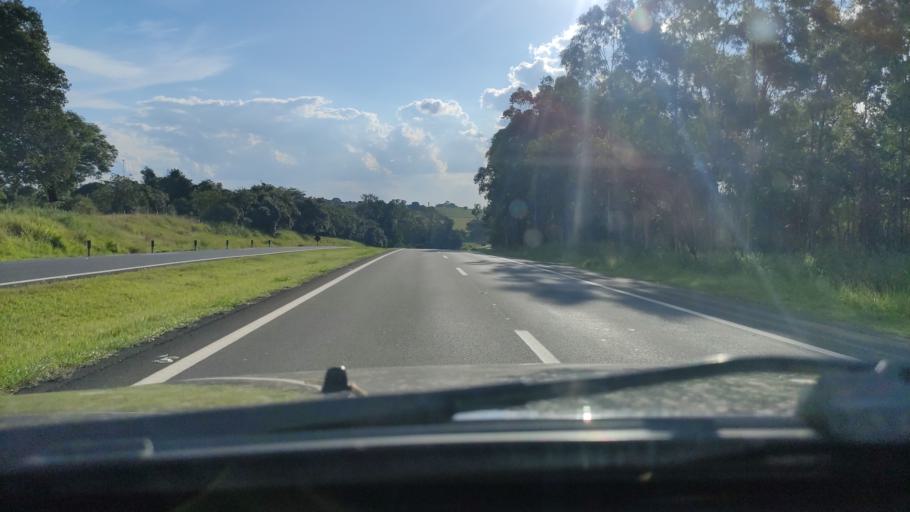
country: BR
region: Sao Paulo
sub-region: Itapira
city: Itapira
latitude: -22.4530
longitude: -46.8694
